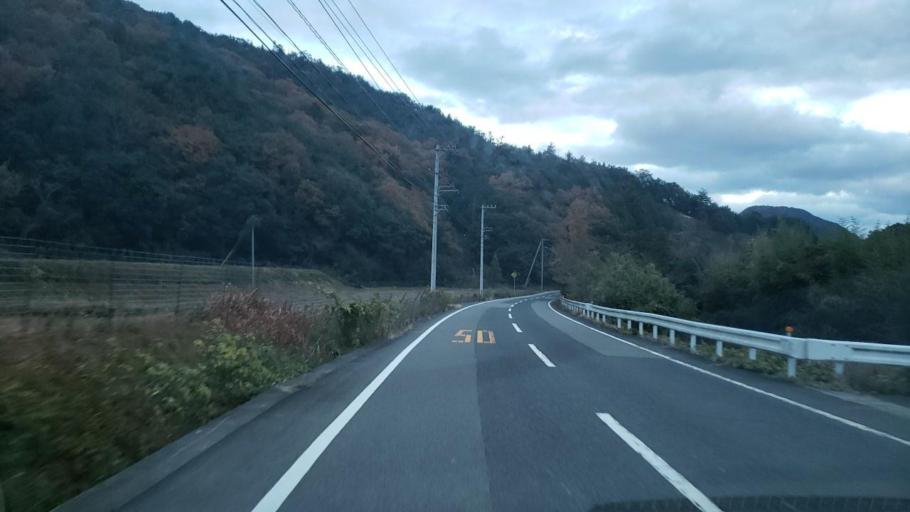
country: JP
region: Tokushima
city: Kamojimacho-jogejima
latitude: 34.1980
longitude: 134.2860
